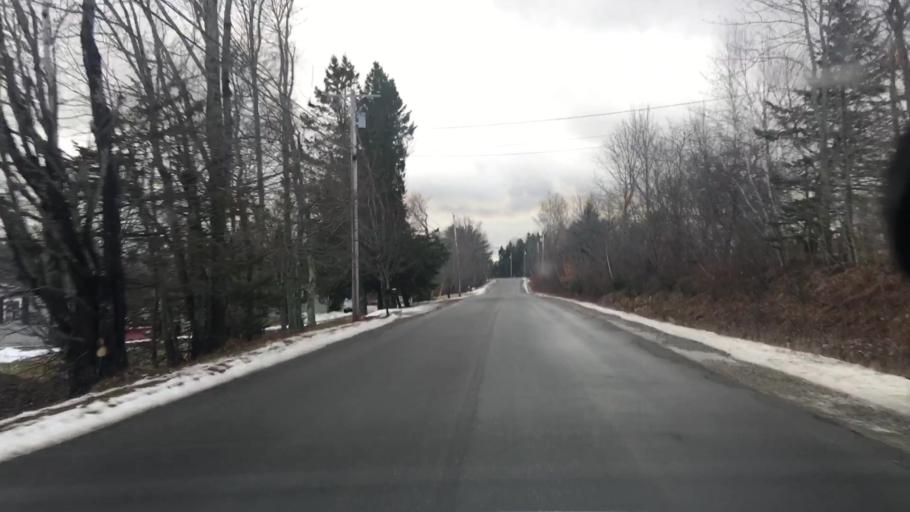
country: US
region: Maine
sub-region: Hancock County
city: Dedham
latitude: 44.6626
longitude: -68.7037
